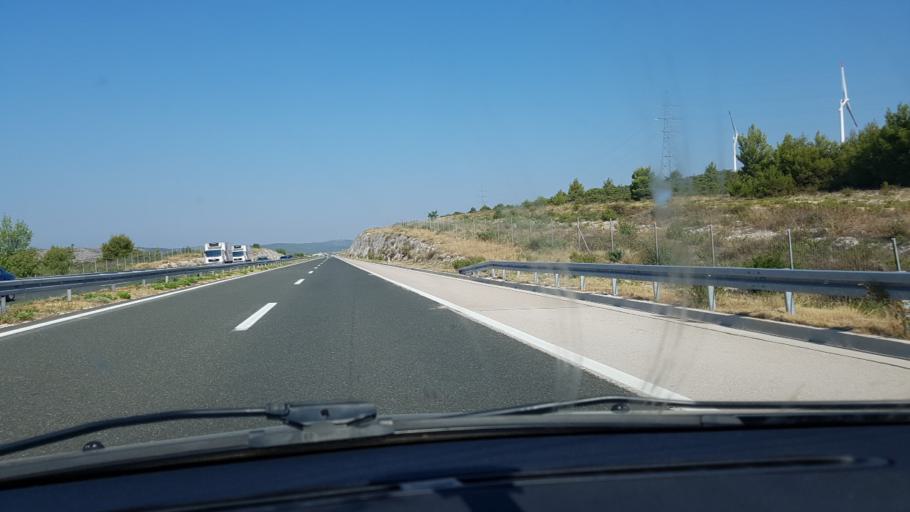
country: HR
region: Sibensko-Kniniska
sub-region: Grad Sibenik
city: Brodarica
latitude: 43.7035
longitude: 16.0091
